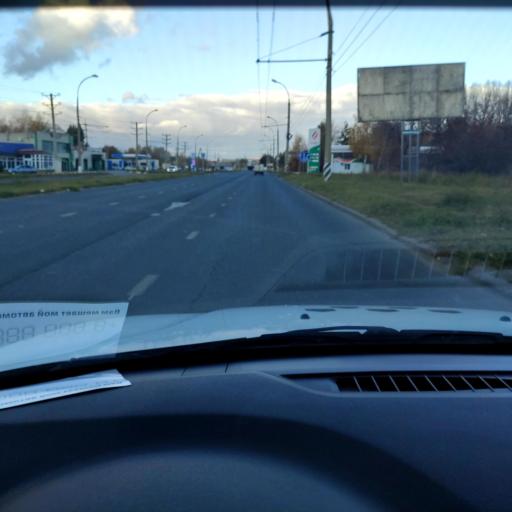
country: RU
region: Samara
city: Tol'yatti
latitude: 53.5482
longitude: 49.3023
